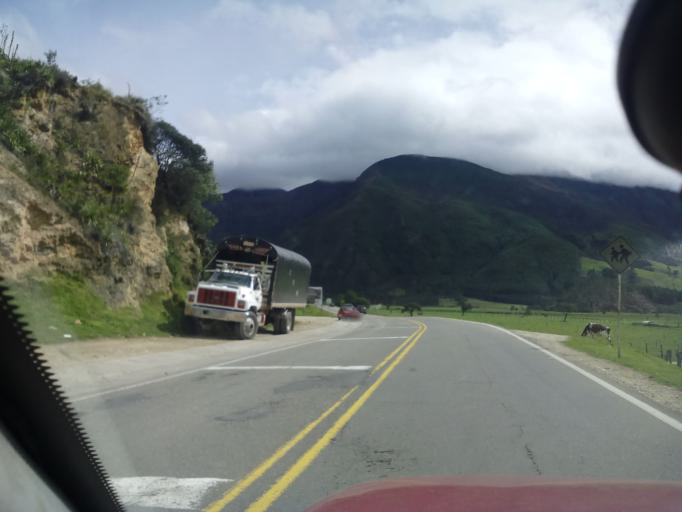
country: CO
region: Boyaca
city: Arcabuco
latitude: 5.7079
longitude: -73.3727
